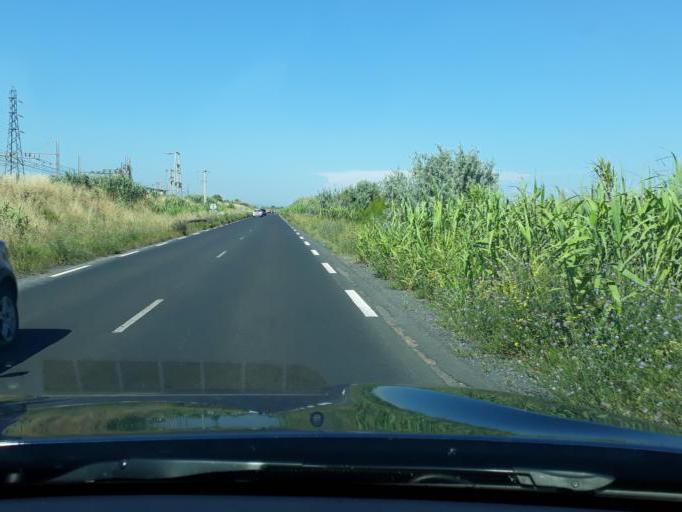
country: FR
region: Languedoc-Roussillon
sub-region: Departement de l'Herault
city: Marseillan
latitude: 43.3345
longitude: 3.5672
